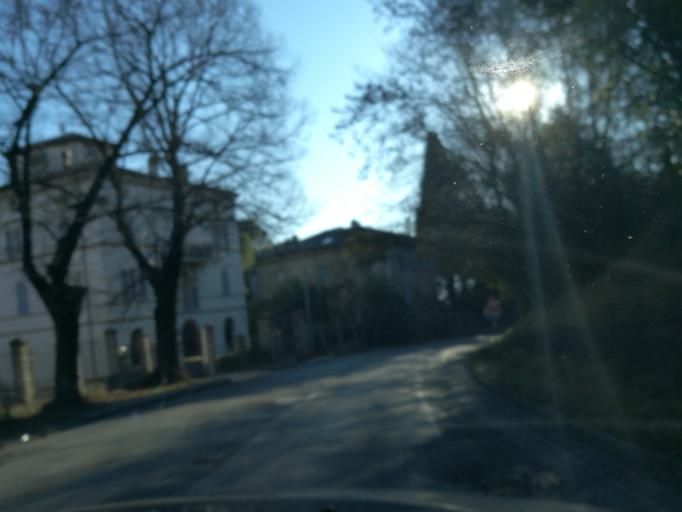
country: IT
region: Umbria
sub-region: Provincia di Perugia
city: Perugia
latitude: 43.0943
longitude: 12.3999
